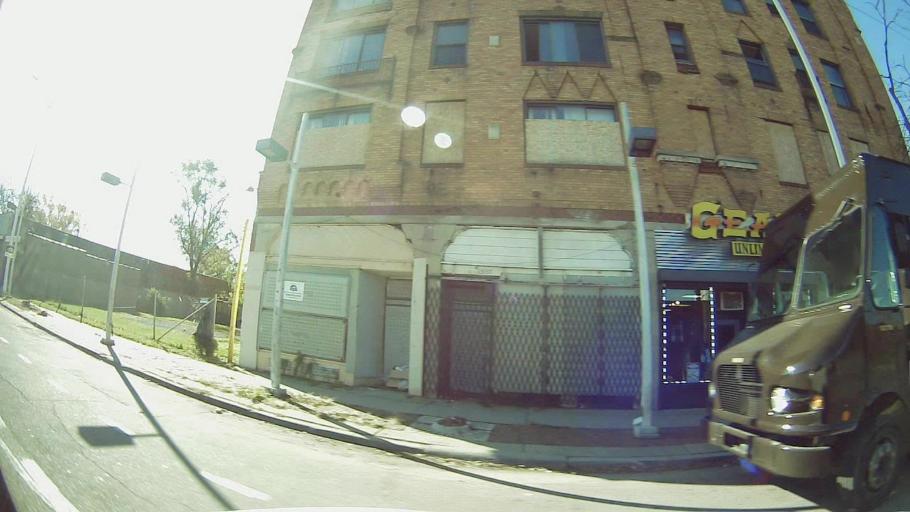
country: US
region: Michigan
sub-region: Wayne County
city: Highland Park
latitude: 42.3875
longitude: -83.1295
